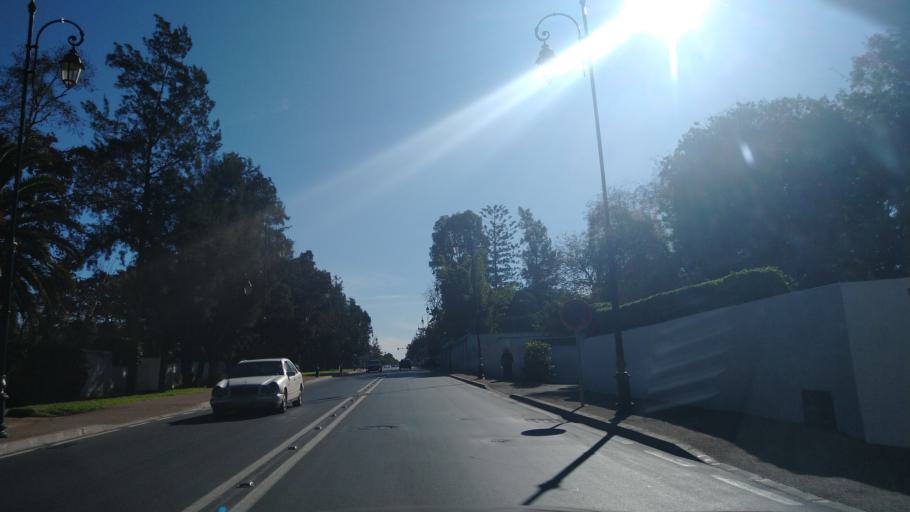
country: MA
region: Rabat-Sale-Zemmour-Zaer
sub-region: Rabat
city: Rabat
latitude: 33.9784
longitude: -6.8407
